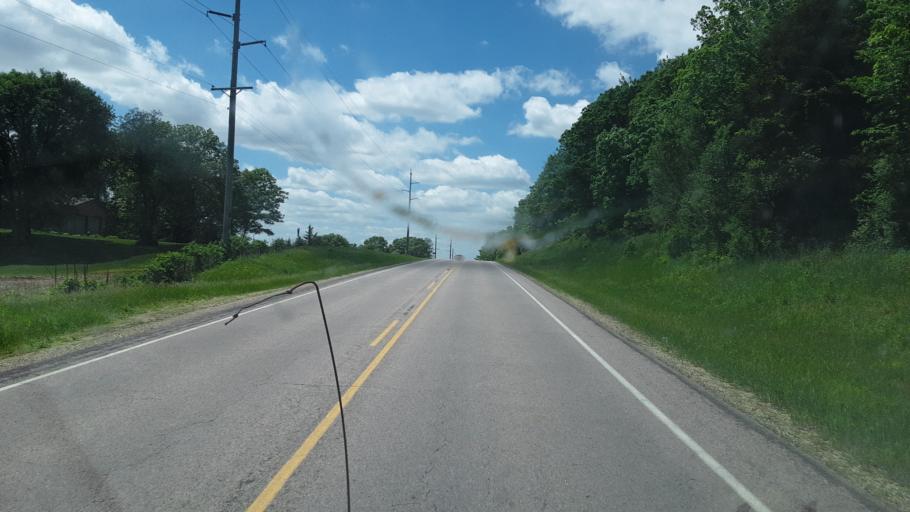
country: US
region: Wisconsin
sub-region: Sauk County
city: Lake Delton
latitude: 43.5907
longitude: -89.8429
